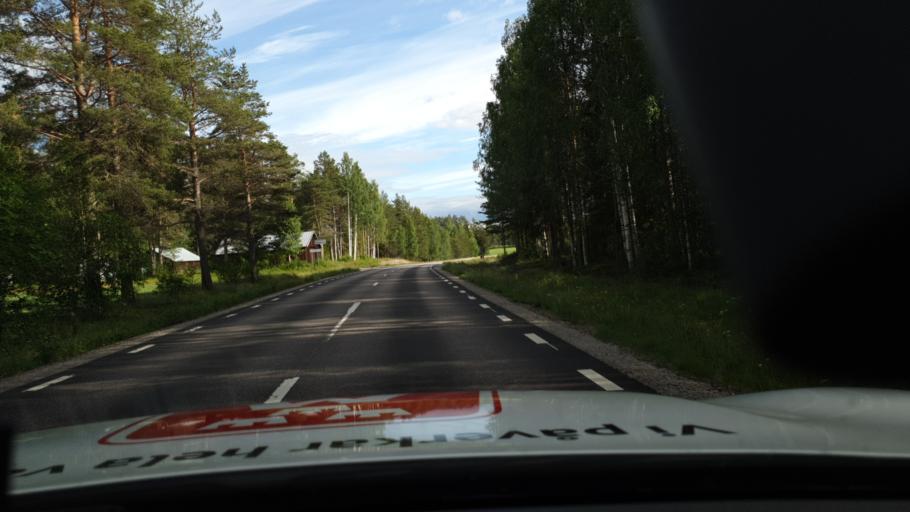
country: SE
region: Norrbotten
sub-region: Overkalix Kommun
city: OEverkalix
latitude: 66.4359
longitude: 22.7928
